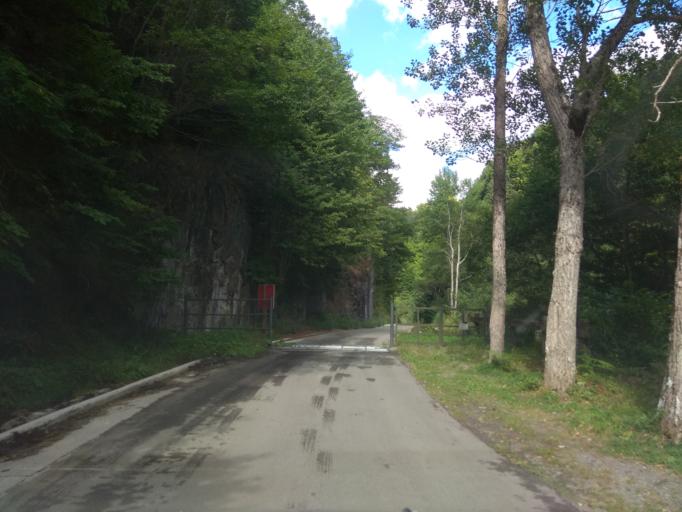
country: ES
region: Catalonia
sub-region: Provincia de Lleida
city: Vielha
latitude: 42.7177
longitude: 0.7231
